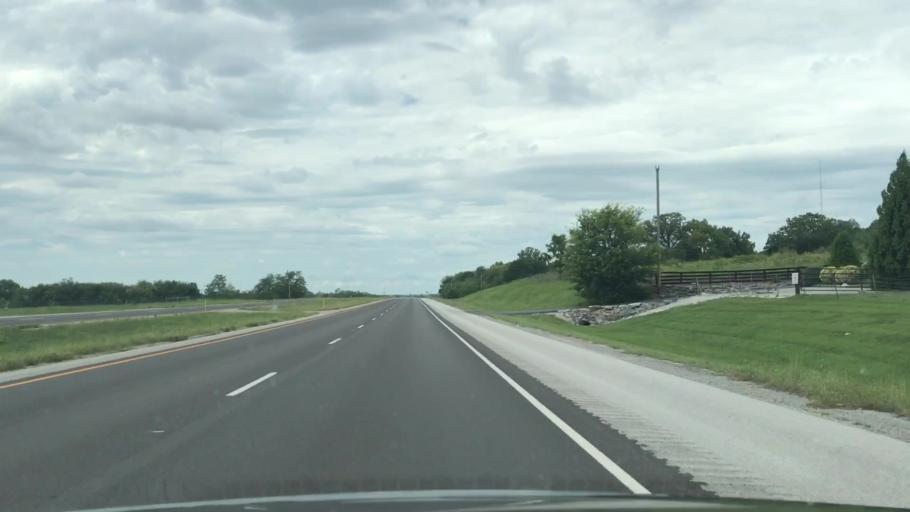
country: US
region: Kentucky
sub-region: Todd County
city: Elkton
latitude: 36.8082
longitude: -87.1251
